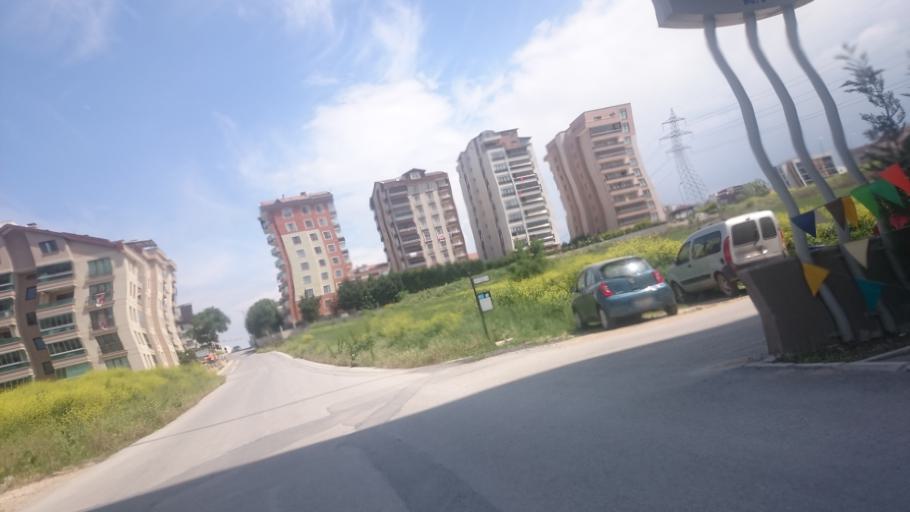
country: TR
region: Bursa
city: Cali
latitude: 40.2187
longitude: 28.9462
